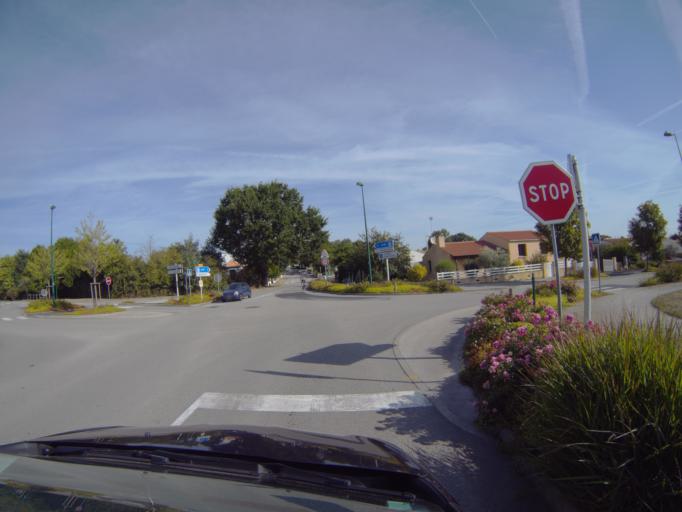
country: FR
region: Pays de la Loire
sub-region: Departement de la Vendee
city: Les Clouzeaux
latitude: 46.6338
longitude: -1.5097
